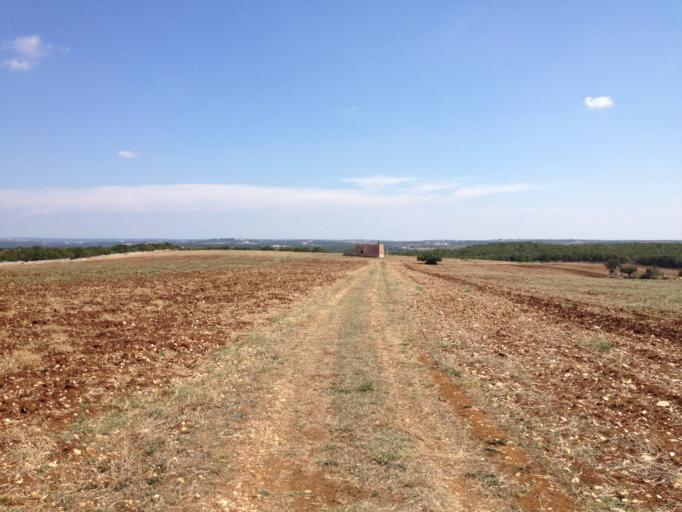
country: IT
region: Apulia
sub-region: Provincia di Bari
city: Gioia del Colle
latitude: 40.8247
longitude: 16.9962
